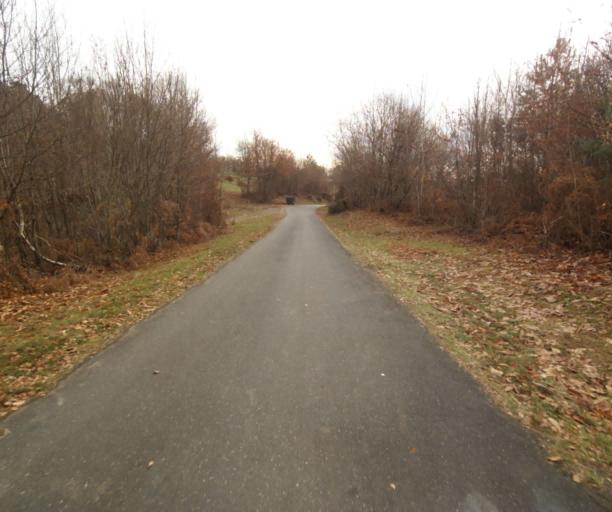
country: FR
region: Limousin
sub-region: Departement de la Correze
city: Chameyrat
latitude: 45.2602
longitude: 1.7059
